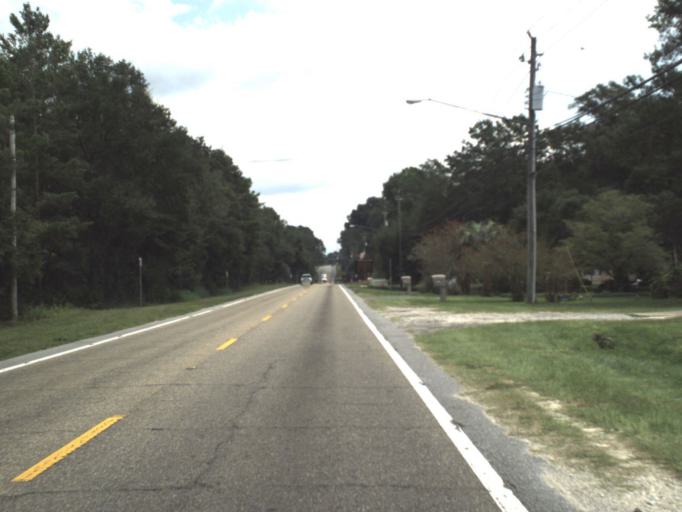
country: US
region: Florida
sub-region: Bay County
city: Hiland Park
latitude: 30.2333
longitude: -85.6035
